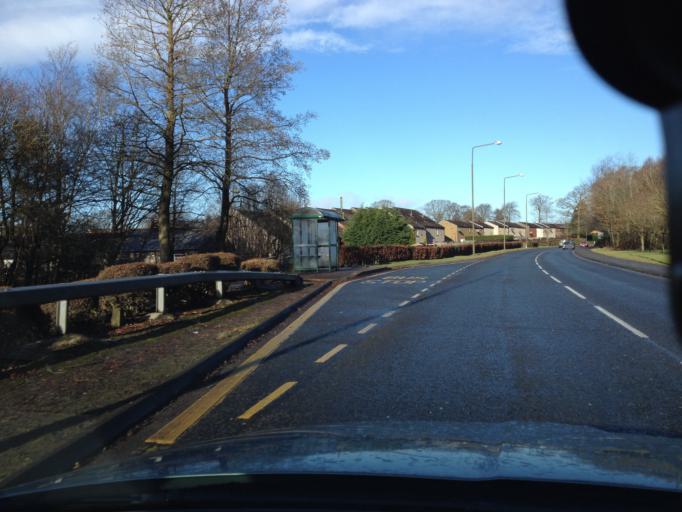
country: GB
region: Scotland
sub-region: West Lothian
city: Livingston
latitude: 55.8945
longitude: -3.5305
